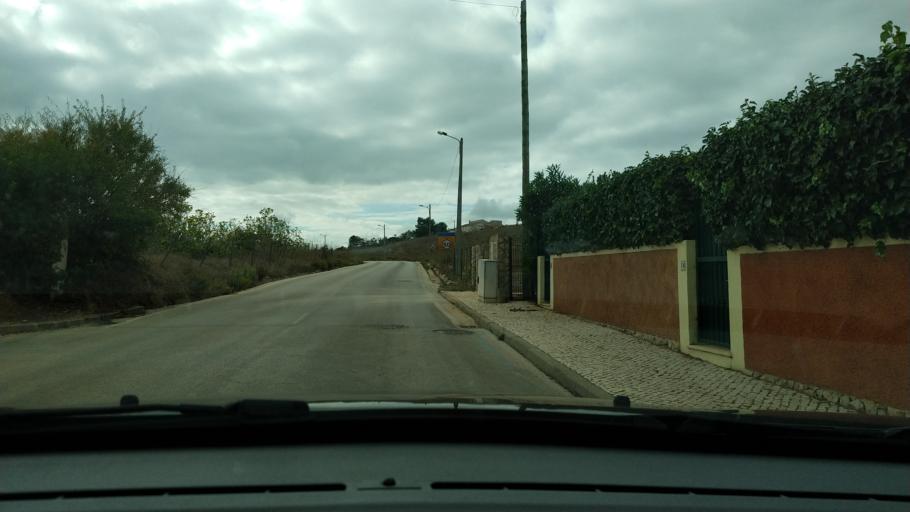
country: PT
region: Faro
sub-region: Lagos
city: Lagos
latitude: 37.0725
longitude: -8.7791
